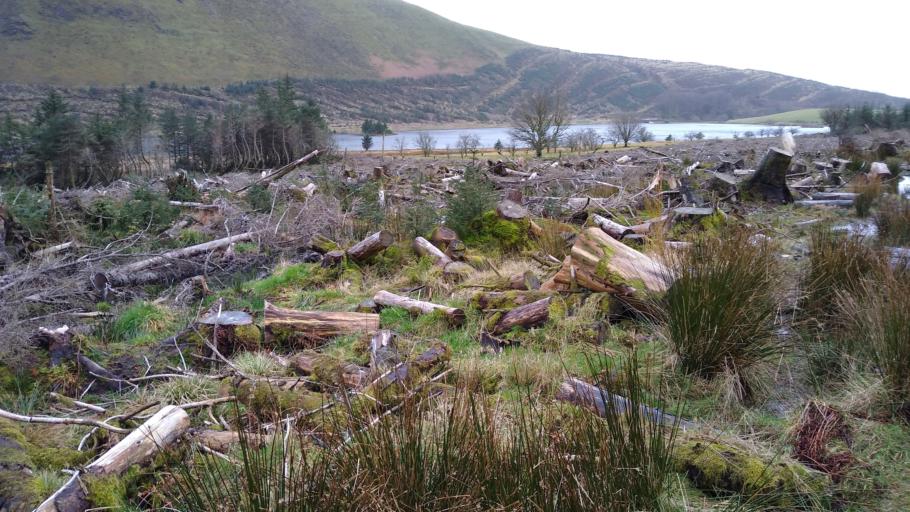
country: GB
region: England
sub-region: Cumbria
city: Frizington
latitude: 54.5650
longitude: -3.3949
